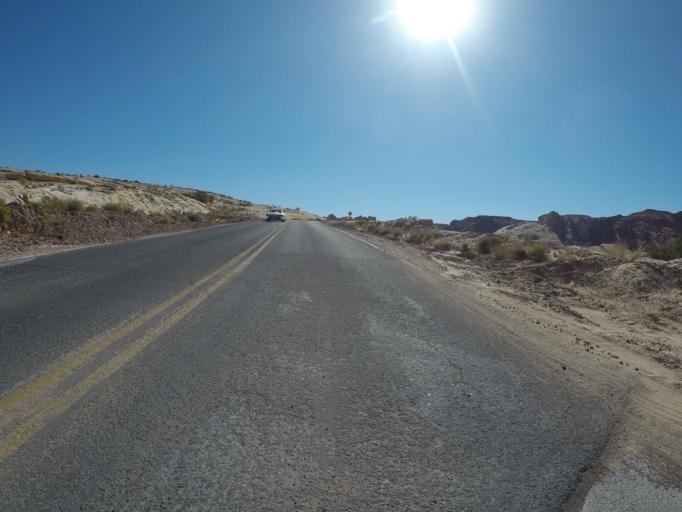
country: US
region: Nevada
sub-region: Clark County
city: Moapa Valley
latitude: 36.4664
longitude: -114.5245
